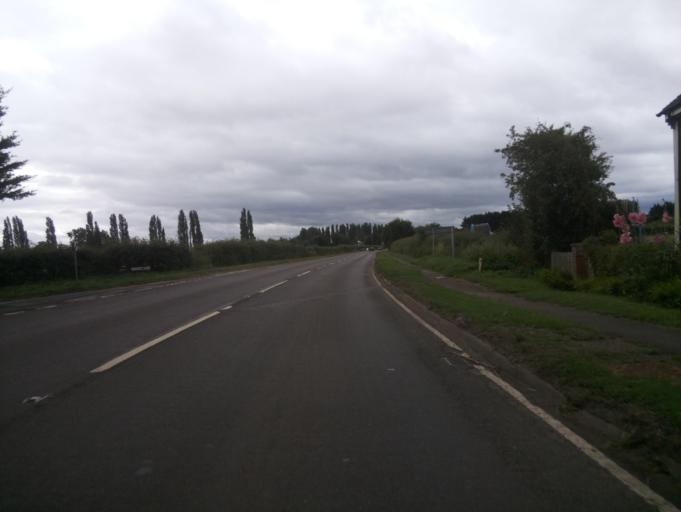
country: GB
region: England
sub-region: Worcestershire
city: Kempsey
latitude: 52.1305
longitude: -2.2152
